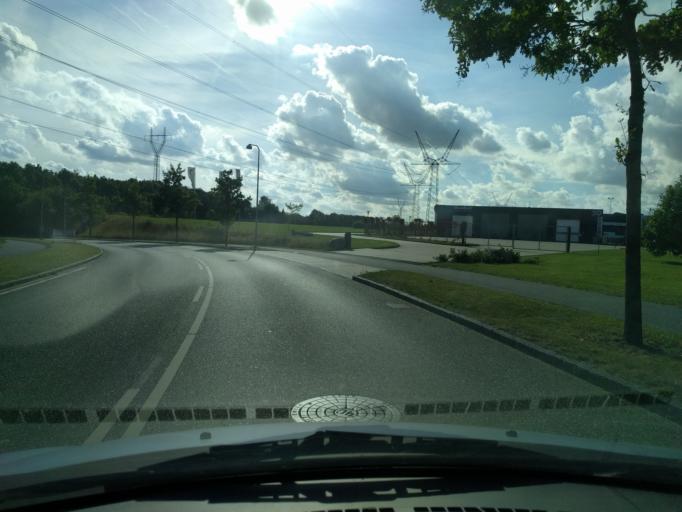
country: DK
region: South Denmark
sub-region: Odense Kommune
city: Neder Holluf
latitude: 55.3626
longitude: 10.4965
